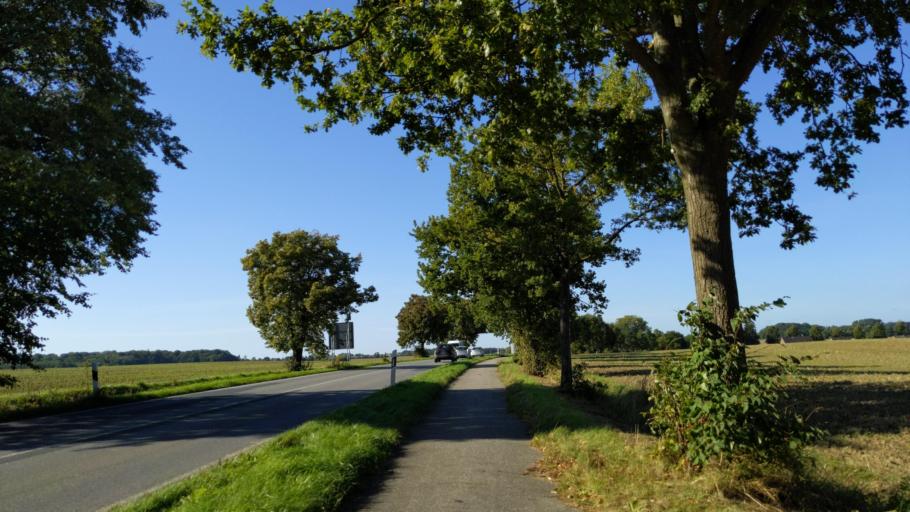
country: DE
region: Schleswig-Holstein
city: Ahrensbok
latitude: 53.9636
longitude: 10.6048
